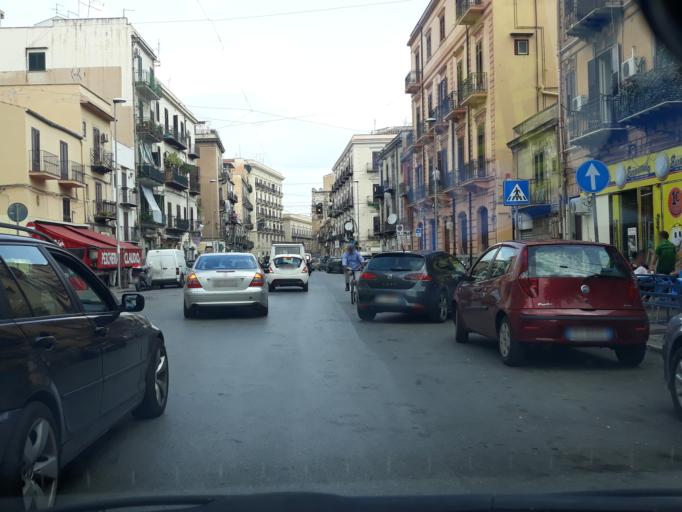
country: IT
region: Sicily
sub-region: Palermo
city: Palermo
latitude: 38.1109
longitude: 13.3690
